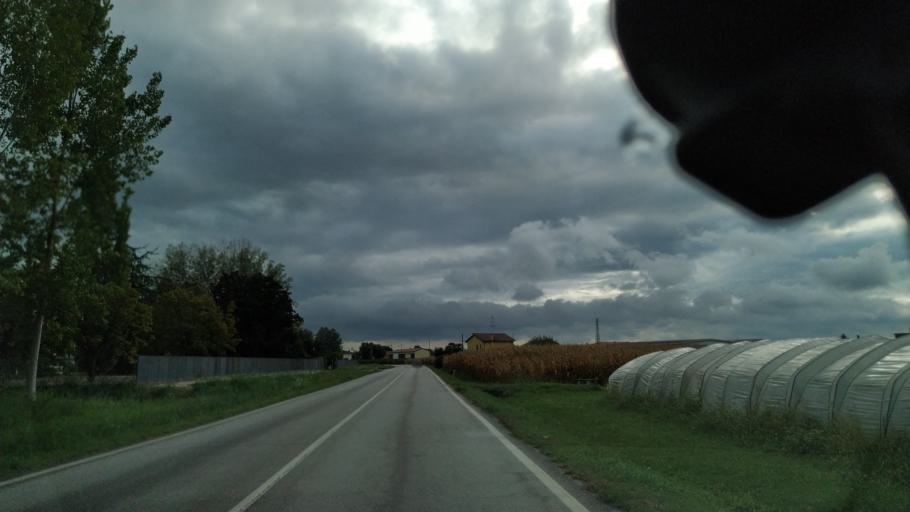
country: IT
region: Emilia-Romagna
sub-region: Provincia di Ferrara
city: Dosso
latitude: 44.7824
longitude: 11.3605
